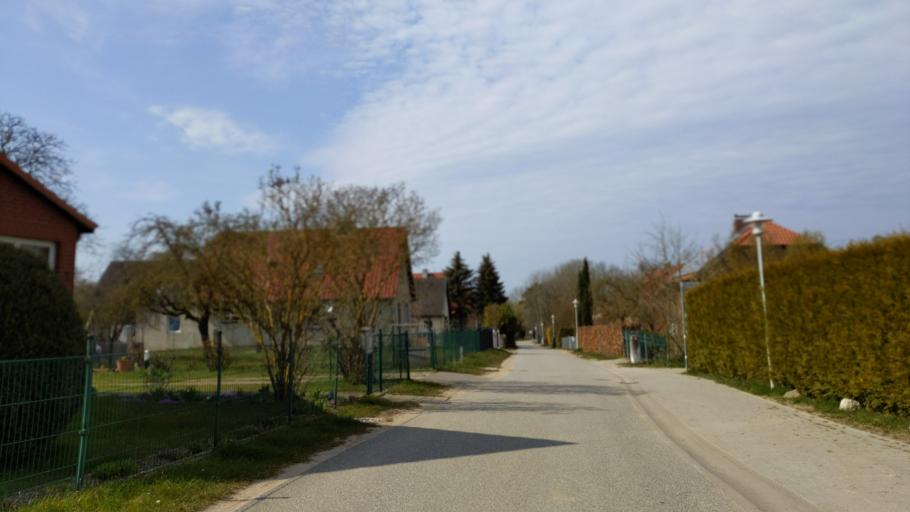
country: DE
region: Mecklenburg-Vorpommern
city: Dassow
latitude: 53.9608
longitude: 10.9407
